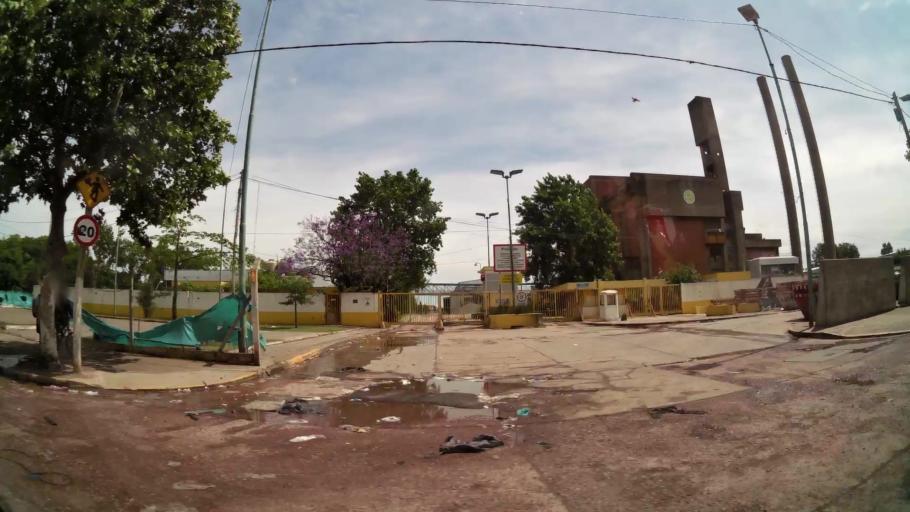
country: AR
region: Buenos Aires F.D.
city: Villa Lugano
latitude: -34.6544
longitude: -58.4400
